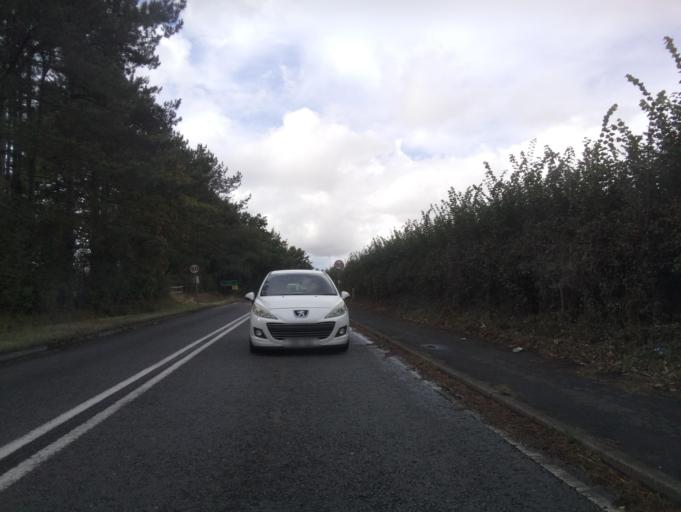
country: GB
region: England
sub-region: Worcestershire
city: Kidderminster
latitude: 52.3661
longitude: -2.1938
